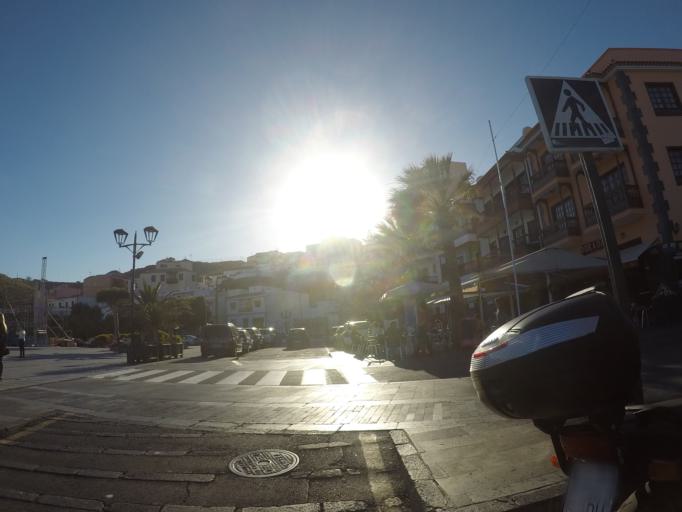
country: ES
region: Canary Islands
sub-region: Provincia de Santa Cruz de Tenerife
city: Candelaria
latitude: 28.3522
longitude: -16.3698
